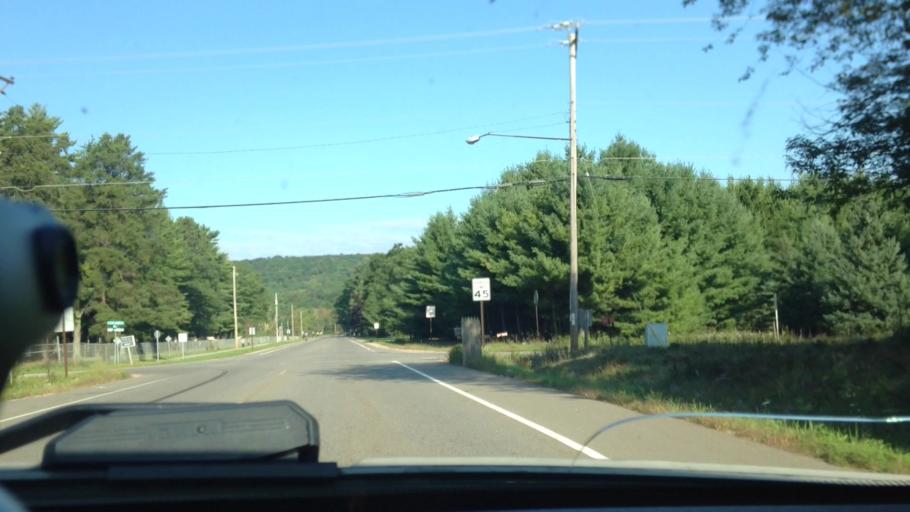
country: US
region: Michigan
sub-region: Dickinson County
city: Quinnesec
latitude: 45.8390
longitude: -88.0125
